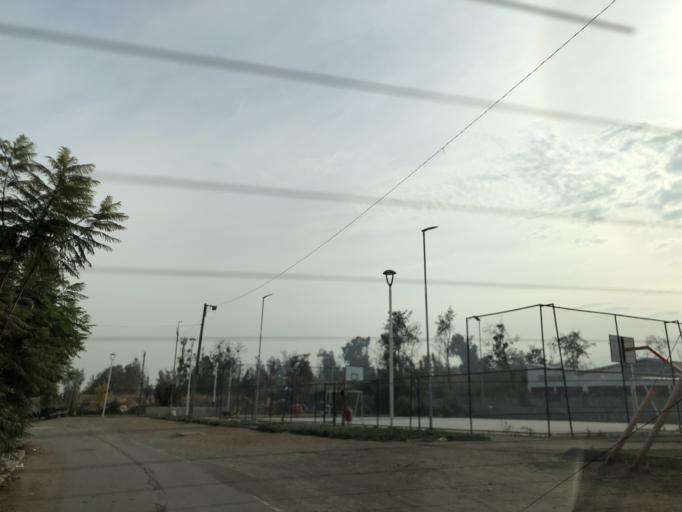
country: CL
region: Santiago Metropolitan
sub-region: Provincia de Cordillera
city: Puente Alto
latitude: -33.5848
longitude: -70.5490
